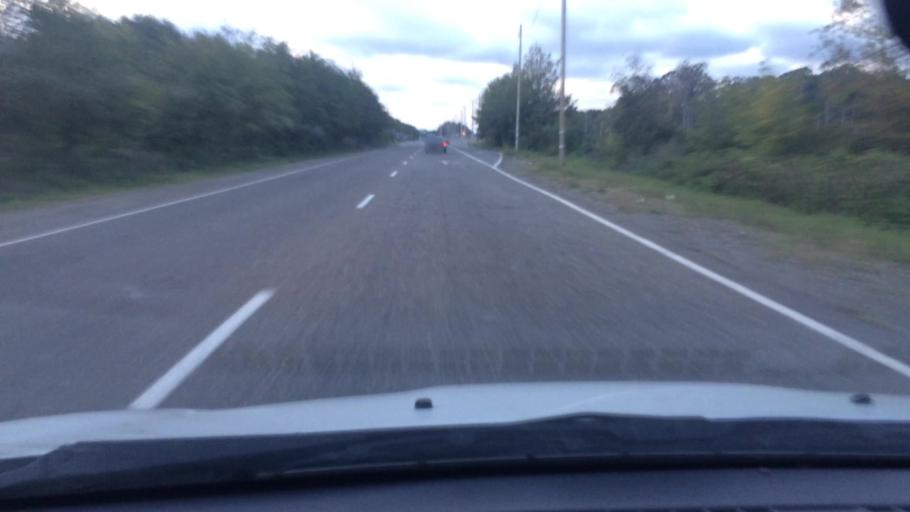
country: GE
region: Guria
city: Urek'i
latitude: 41.9356
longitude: 41.7719
